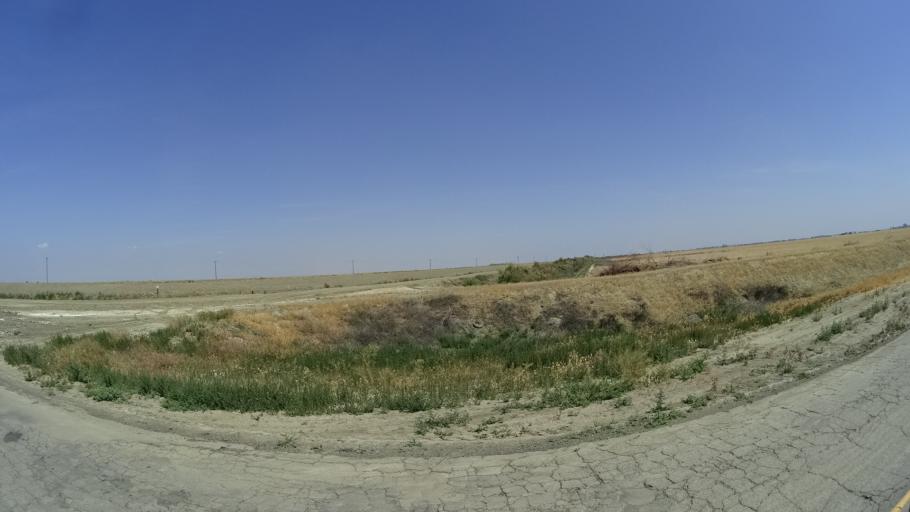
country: US
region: California
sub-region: Kings County
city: Stratford
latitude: 36.1379
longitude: -119.8853
